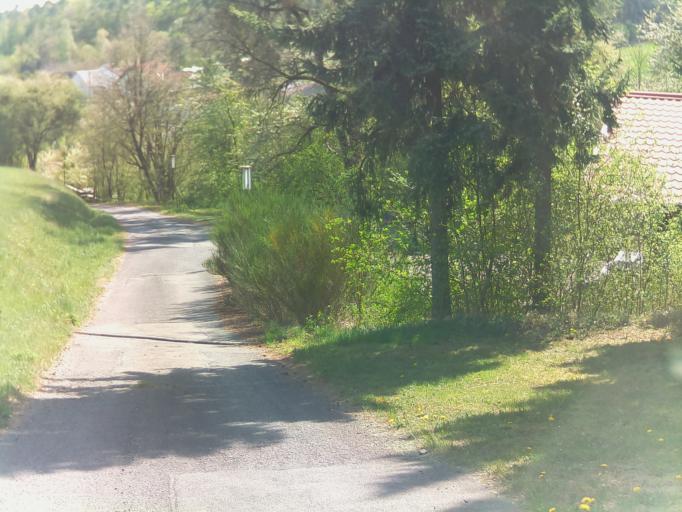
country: DE
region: Bavaria
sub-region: Regierungsbezirk Unterfranken
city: Burgpreppach
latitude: 50.1721
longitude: 10.6310
